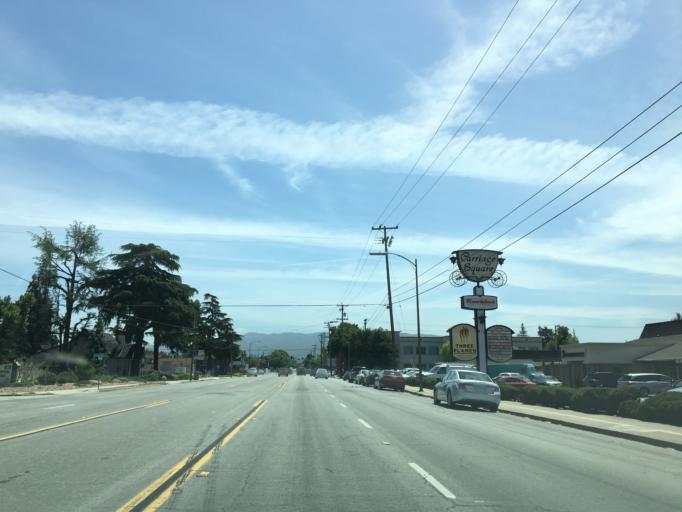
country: US
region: California
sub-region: Santa Clara County
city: Buena Vista
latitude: 37.2969
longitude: -121.9136
